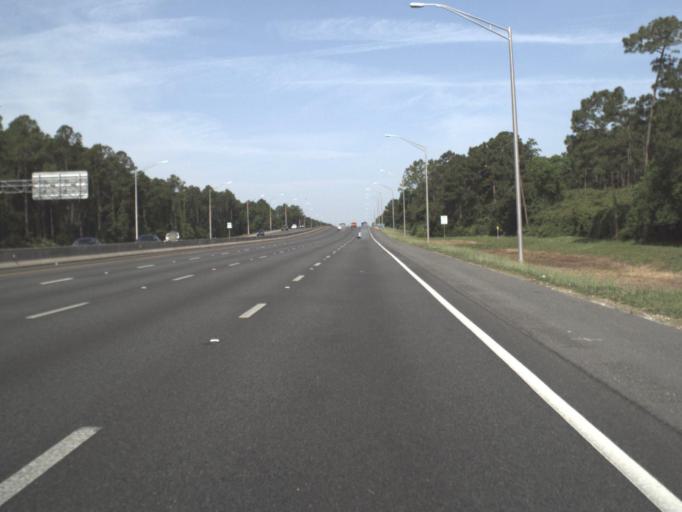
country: US
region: Florida
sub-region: Saint Johns County
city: Ponte Vedra Beach
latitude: 30.2515
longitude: -81.4790
